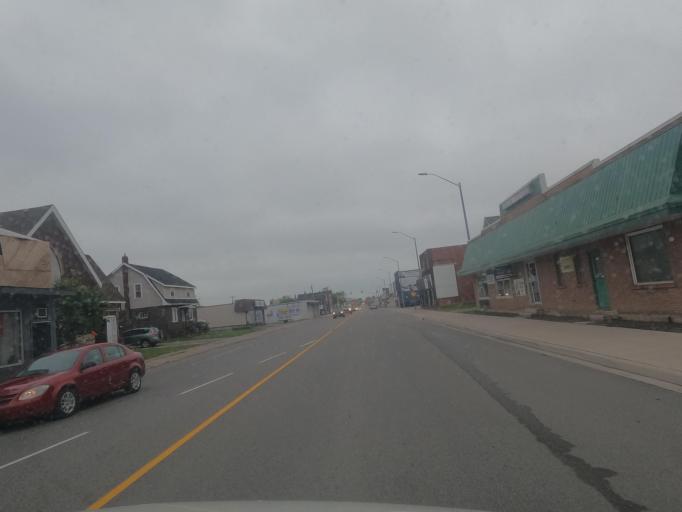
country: CA
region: Ontario
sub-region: Algoma
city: Sault Ste. Marie
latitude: 46.5265
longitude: -84.3478
